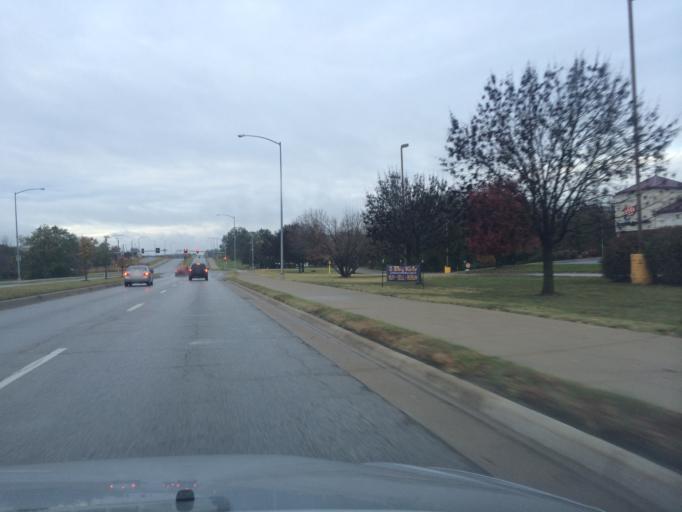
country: US
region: Kansas
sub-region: Douglas County
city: Lawrence
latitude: 38.9427
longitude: -95.2815
